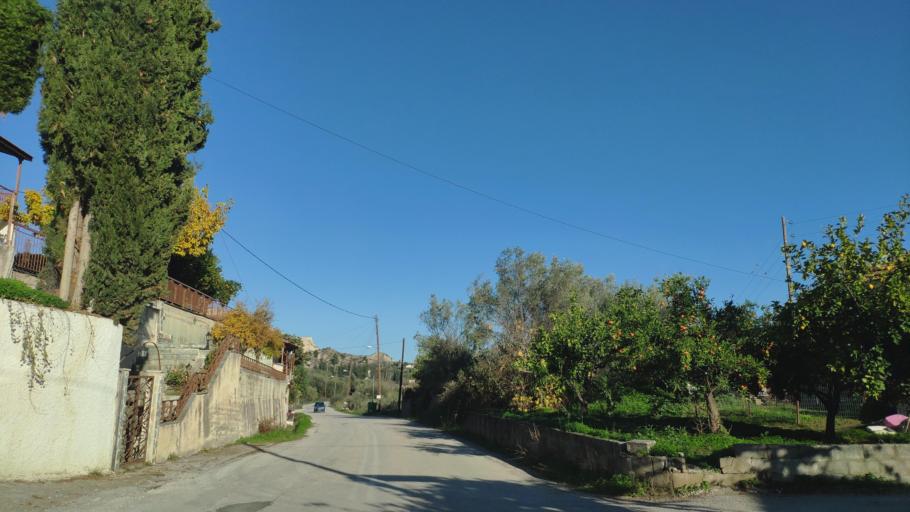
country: GR
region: Peloponnese
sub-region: Nomos Korinthias
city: Xylokastro
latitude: 38.0521
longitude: 22.5911
